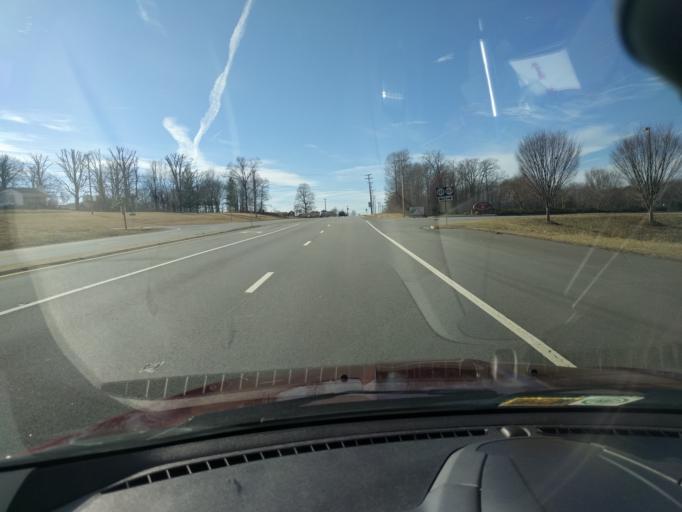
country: US
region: Virginia
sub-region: Amherst County
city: Madison Heights
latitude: 37.4670
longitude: -79.1106
